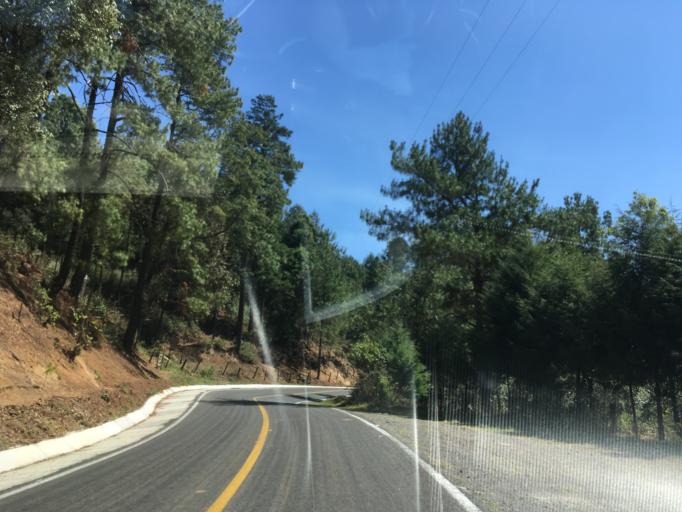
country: MX
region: Michoacan
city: Tzitzio
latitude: 19.6769
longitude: -100.9070
